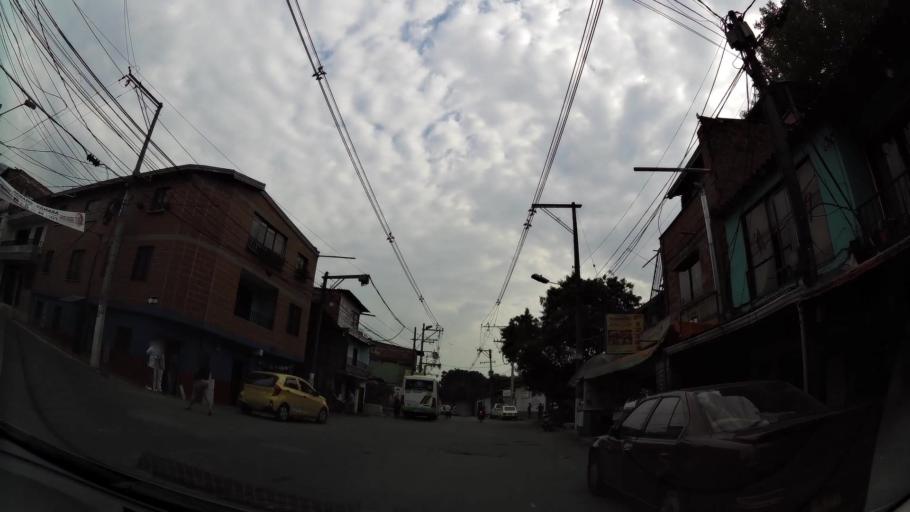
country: CO
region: Antioquia
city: Bello
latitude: 6.3088
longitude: -75.5553
